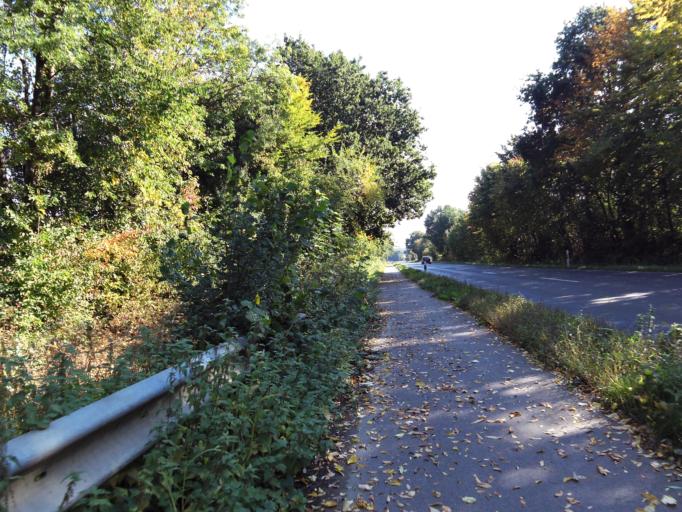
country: DE
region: North Rhine-Westphalia
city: Baesweiler
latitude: 50.9167
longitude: 6.1546
